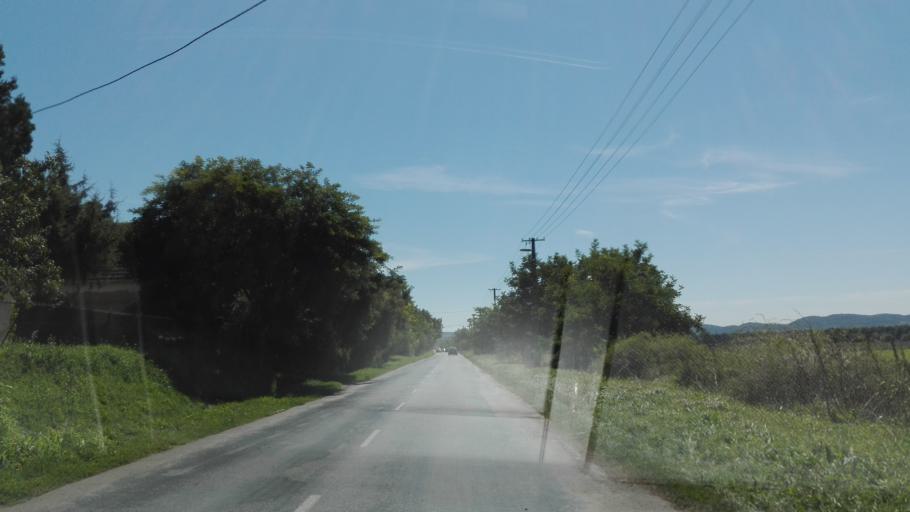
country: HU
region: Tolna
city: Ozora
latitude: 46.7525
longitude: 18.4396
